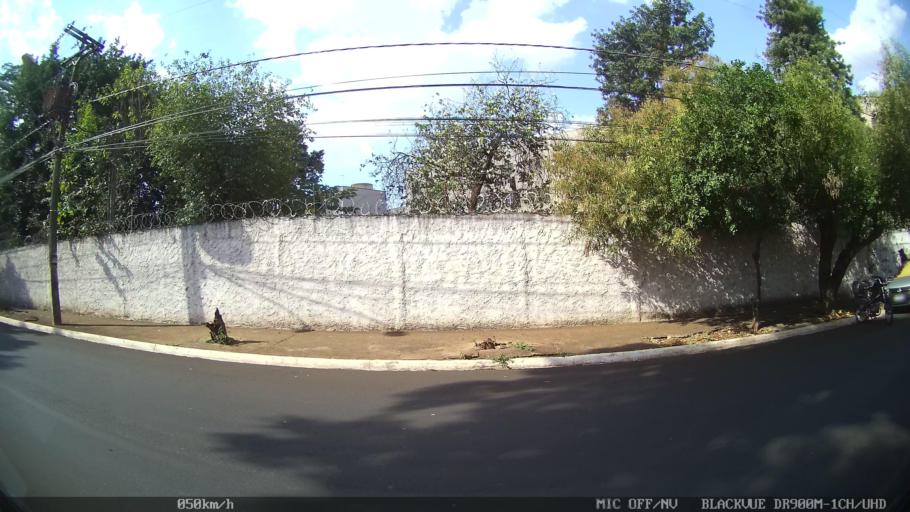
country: BR
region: Sao Paulo
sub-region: Ribeirao Preto
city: Ribeirao Preto
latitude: -21.1922
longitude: -47.8244
